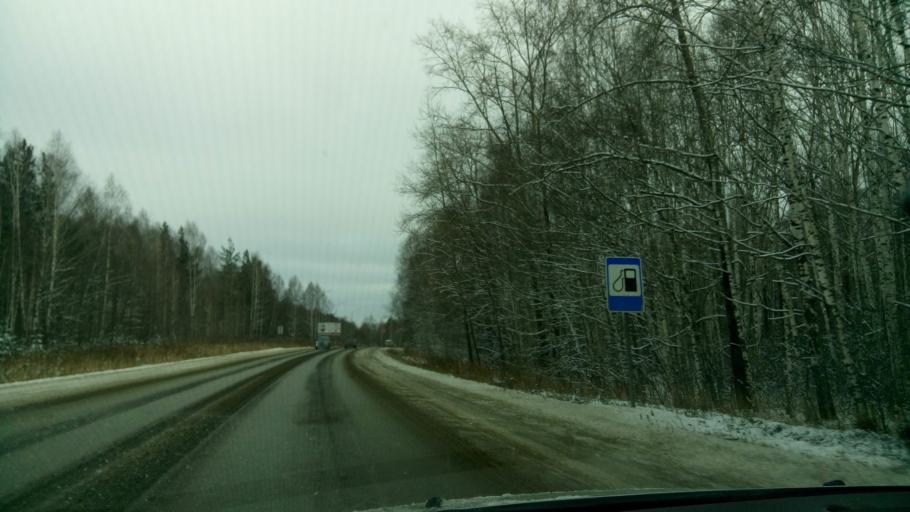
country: RU
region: Sverdlovsk
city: Polevskoy
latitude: 56.4639
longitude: 60.2225
